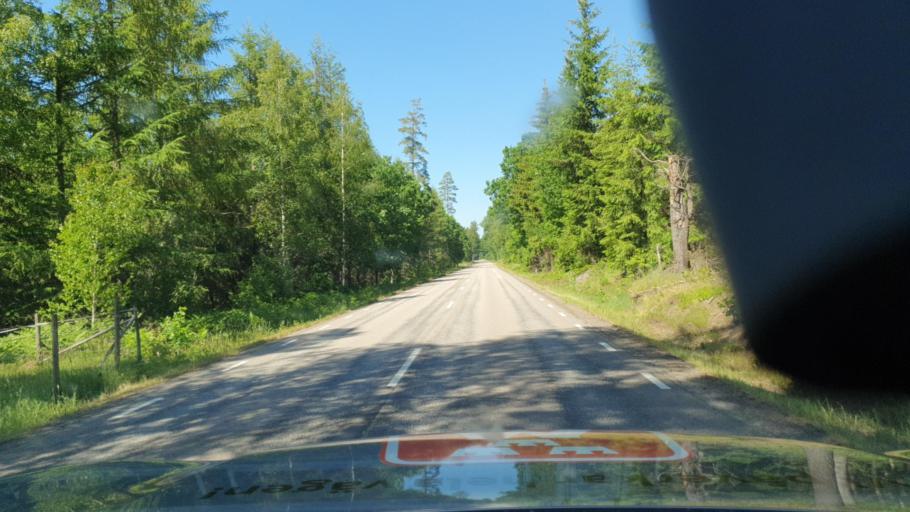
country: SE
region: Kalmar
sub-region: Emmaboda Kommun
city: Emmaboda
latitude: 56.4987
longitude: 15.6683
